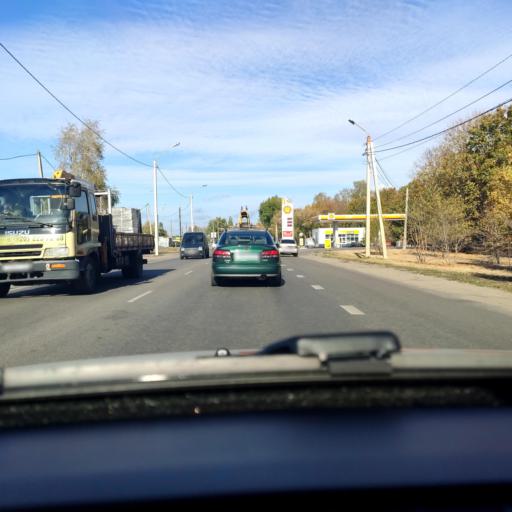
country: RU
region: Voronezj
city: Voronezh
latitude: 51.6162
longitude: 39.1782
